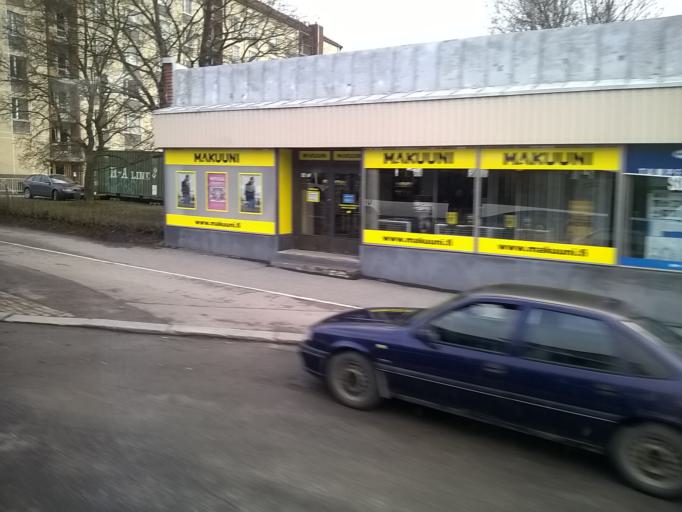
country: FI
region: Pirkanmaa
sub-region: Tampere
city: Tampere
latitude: 61.4964
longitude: 23.8044
